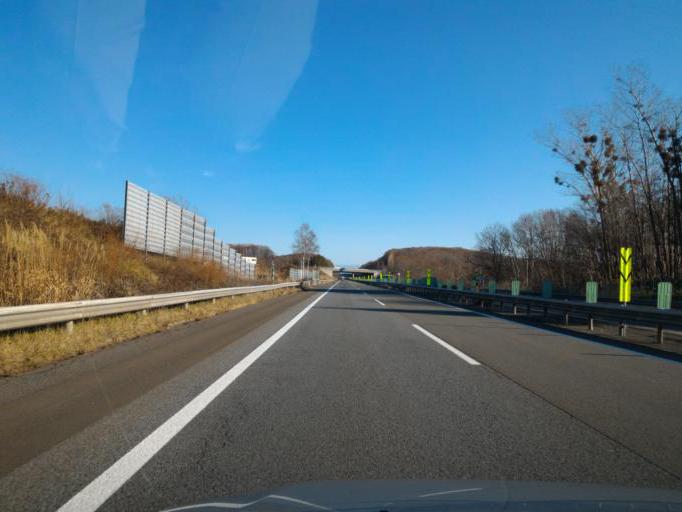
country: JP
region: Hokkaido
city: Iwamizawa
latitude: 43.1803
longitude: 141.7763
